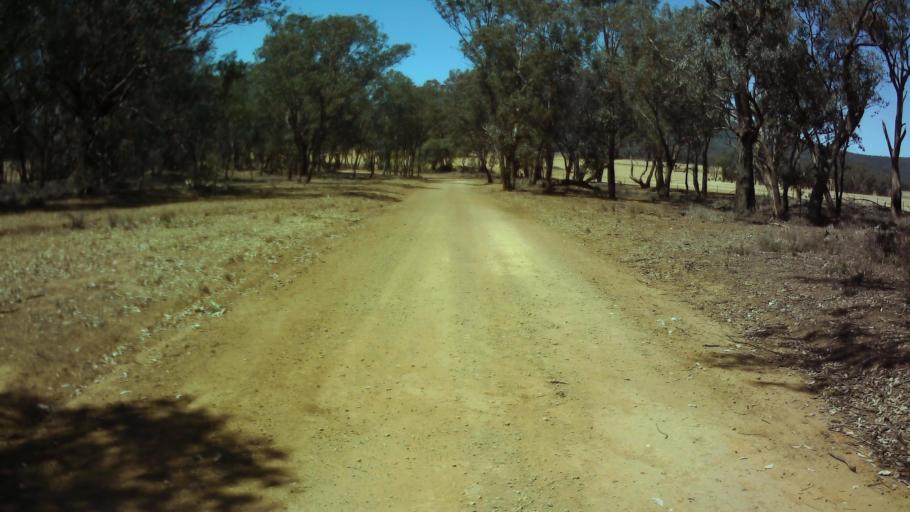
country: AU
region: New South Wales
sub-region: Weddin
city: Grenfell
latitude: -33.9549
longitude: 148.0844
